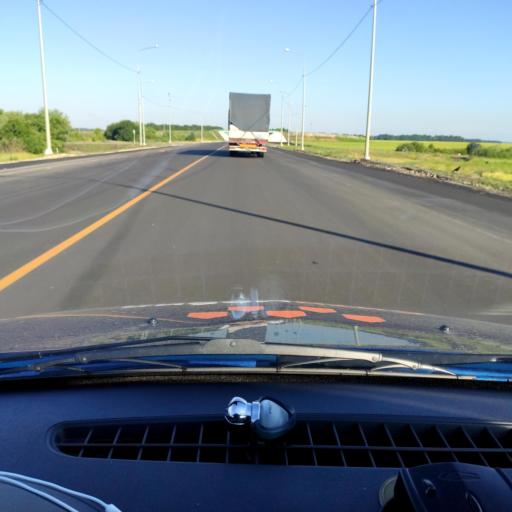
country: RU
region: Orjol
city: Zmiyevka
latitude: 52.6982
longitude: 36.3811
